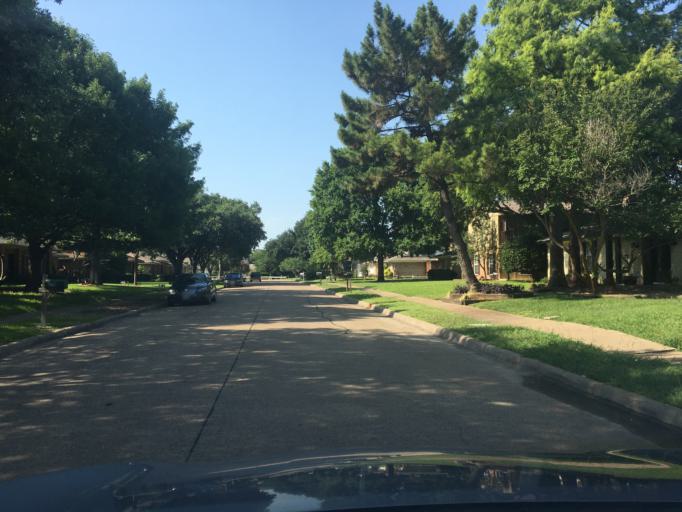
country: US
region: Texas
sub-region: Dallas County
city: Richardson
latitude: 32.9302
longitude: -96.6911
